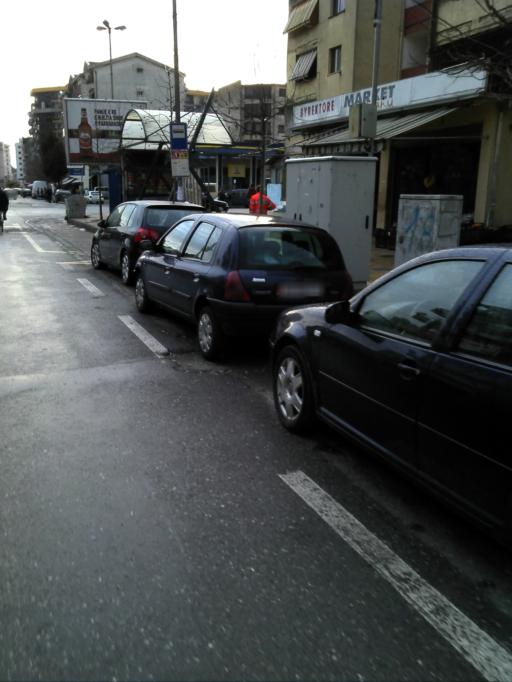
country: AL
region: Shkoder
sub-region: Rrethi i Shkodres
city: Shkoder
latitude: 42.0579
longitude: 19.5023
